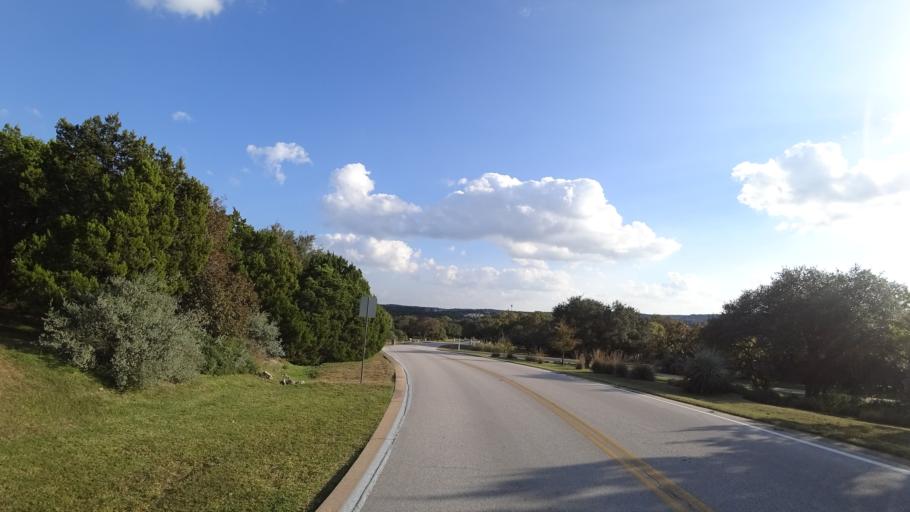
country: US
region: Texas
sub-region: Travis County
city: Barton Creek
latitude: 30.2814
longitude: -97.8718
